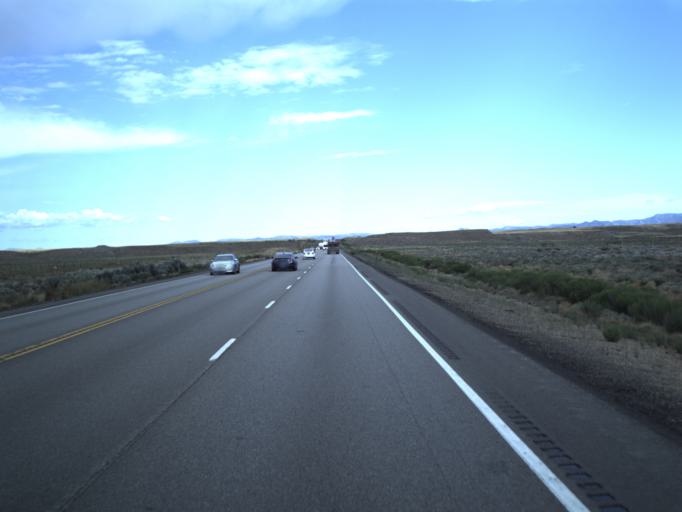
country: US
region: Utah
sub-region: Carbon County
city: East Carbon City
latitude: 39.4931
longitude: -110.5208
